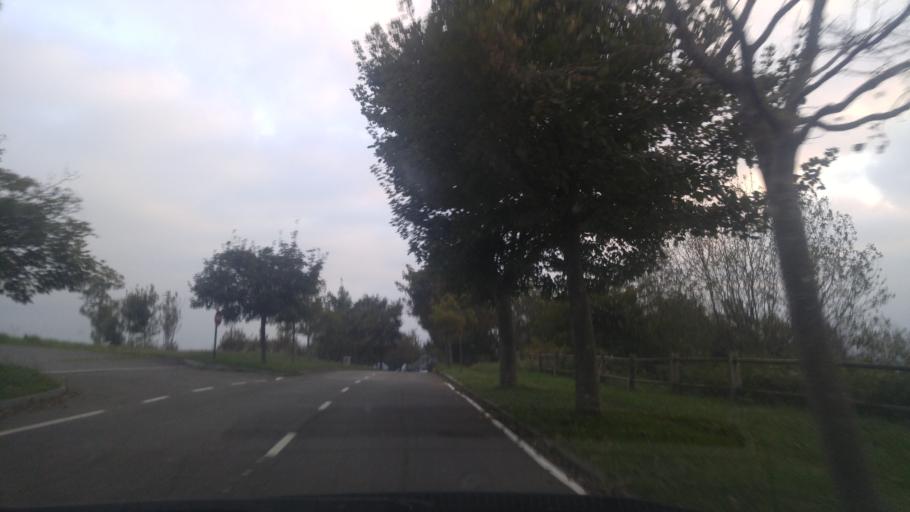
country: ES
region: Asturias
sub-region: Province of Asturias
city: Oviedo
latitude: 43.3857
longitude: -5.8540
